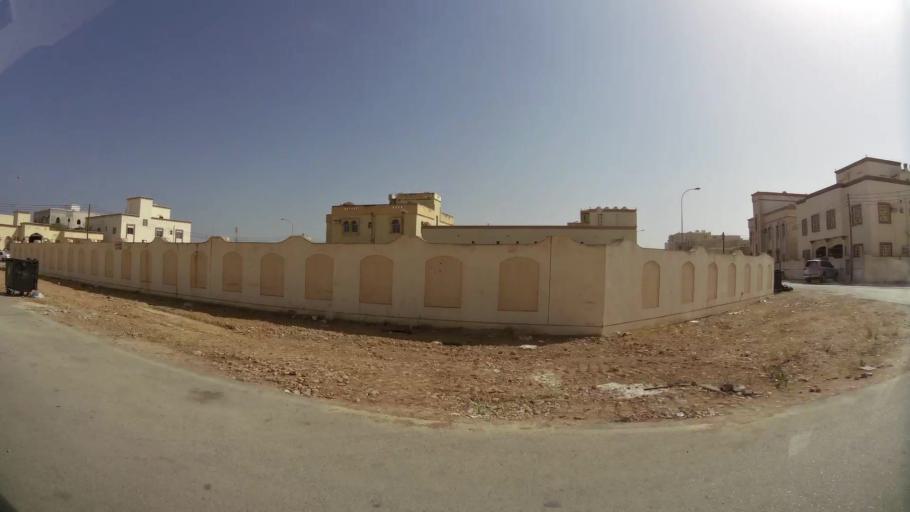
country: OM
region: Zufar
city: Salalah
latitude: 17.0041
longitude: 54.0150
